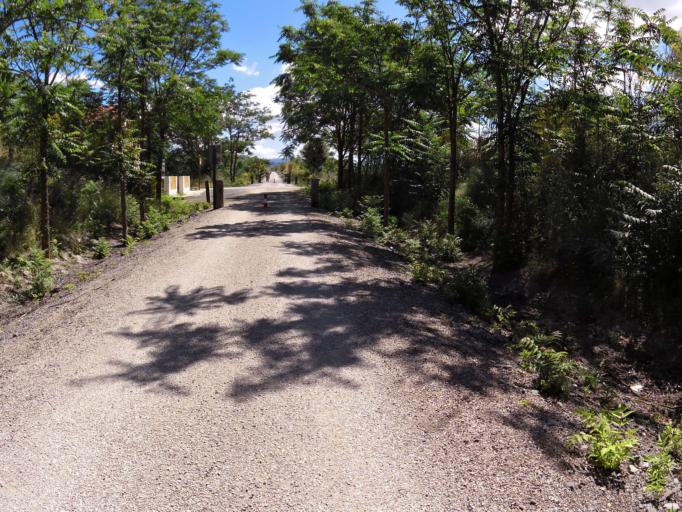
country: ES
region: Andalusia
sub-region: Provincia de Jaen
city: Alcaudete
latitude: 37.6457
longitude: -4.0771
